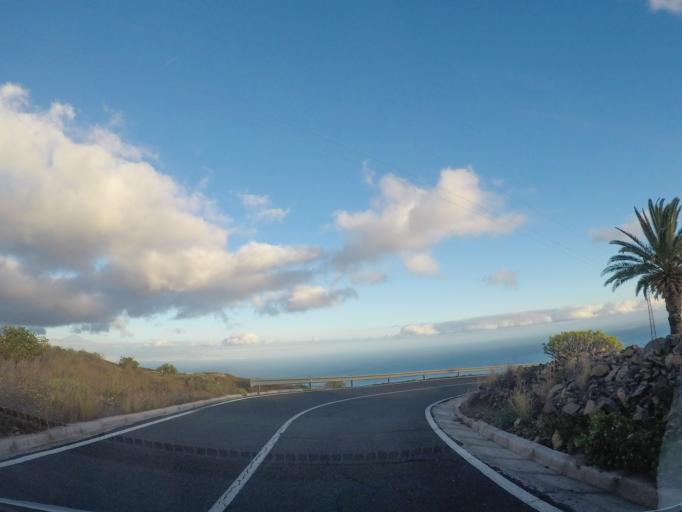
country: ES
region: Canary Islands
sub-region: Provincia de Santa Cruz de Tenerife
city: Alajero
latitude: 28.0480
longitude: -17.2302
